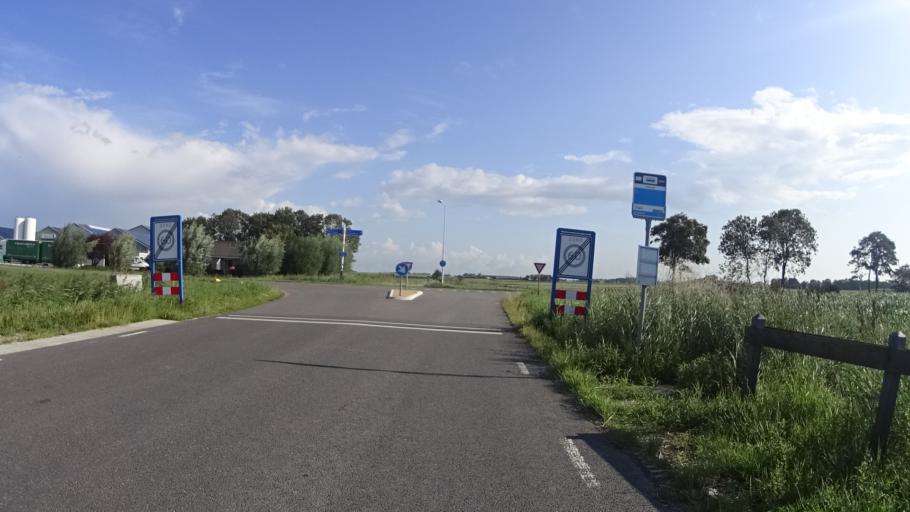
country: NL
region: Friesland
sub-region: Gemeente Harlingen
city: Harlingen
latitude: 53.1358
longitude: 5.4612
